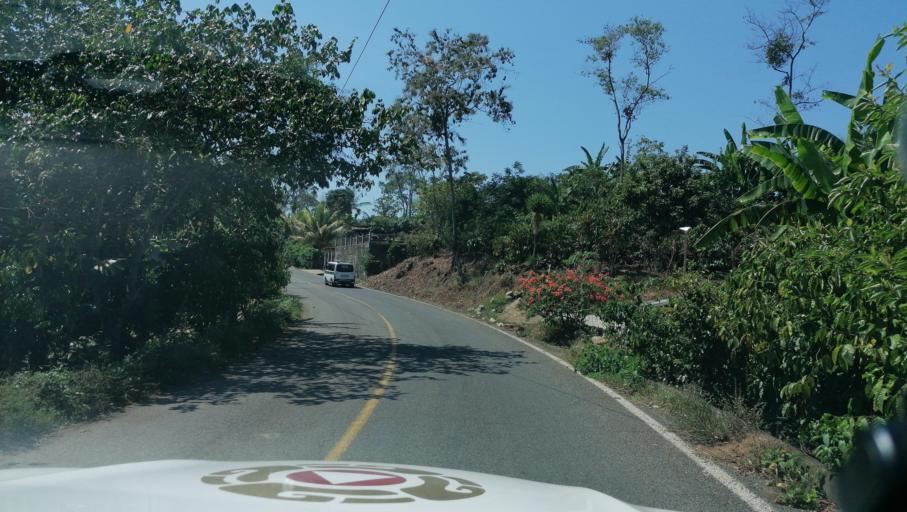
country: MX
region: Chiapas
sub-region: Cacahoatan
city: Benito Juarez
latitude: 15.0176
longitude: -92.2260
